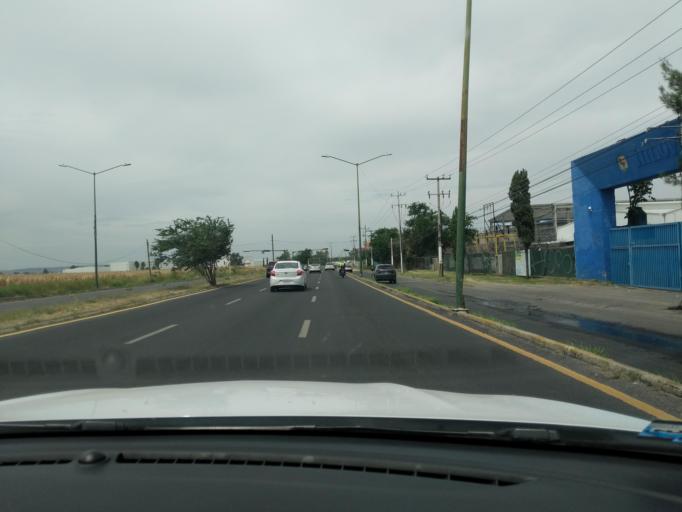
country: MX
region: Jalisco
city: Tesistan
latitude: 20.7890
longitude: -103.4731
